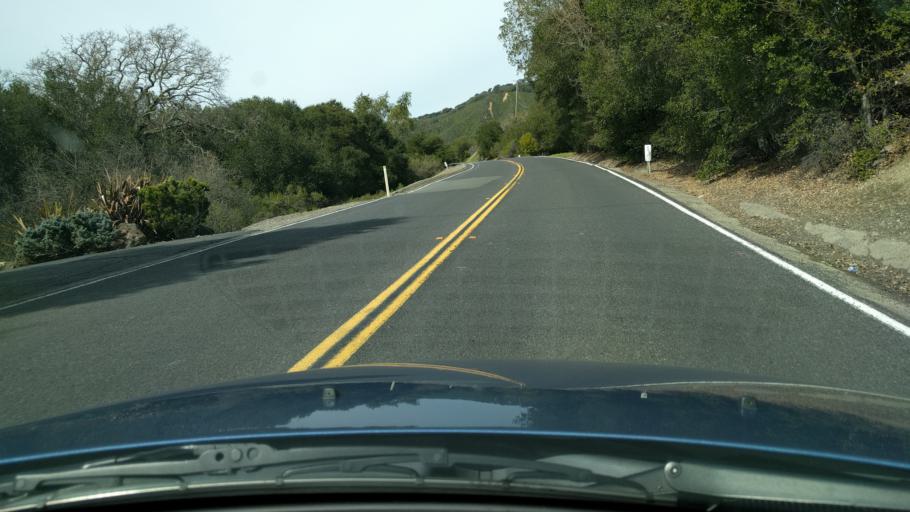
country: US
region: California
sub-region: Contra Costa County
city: San Ramon
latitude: 37.7799
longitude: -121.9991
